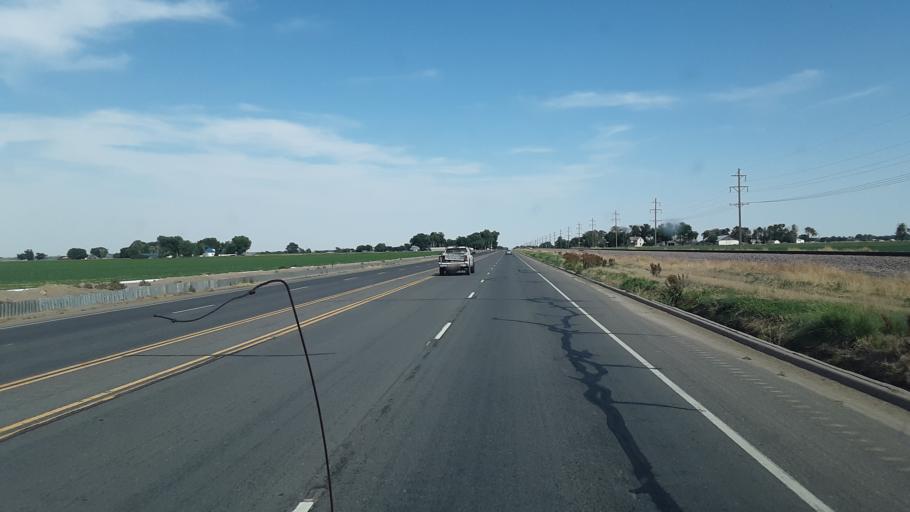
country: US
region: Colorado
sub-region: Otero County
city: Rocky Ford
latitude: 38.0706
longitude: -103.7635
